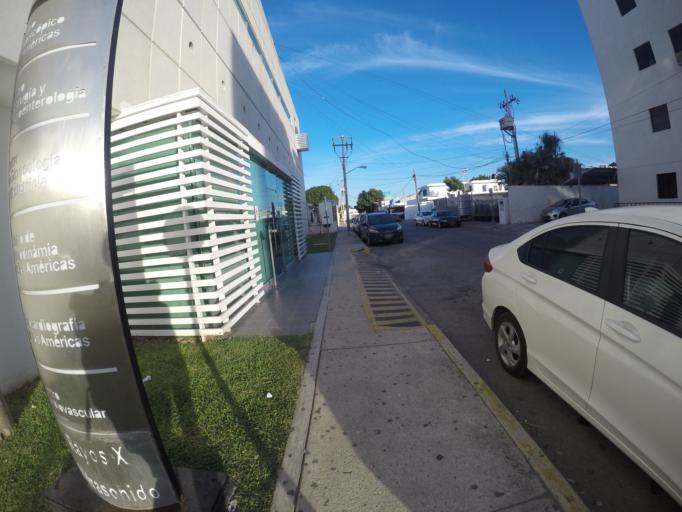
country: MX
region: Yucatan
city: Merida
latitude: 20.9840
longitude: -89.6158
